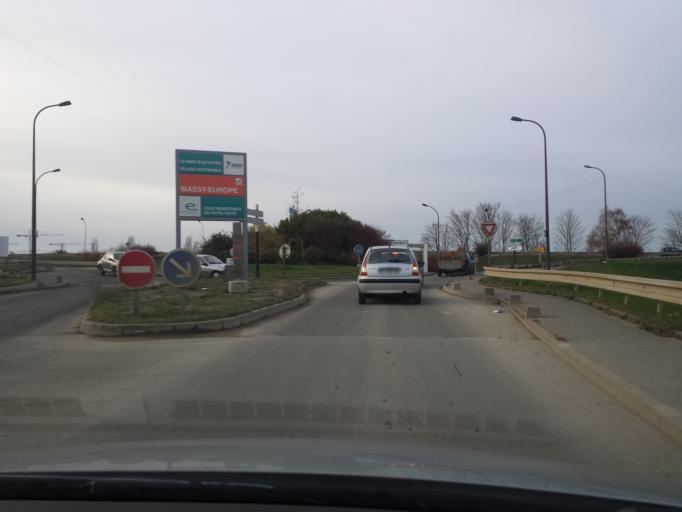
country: FR
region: Ile-de-France
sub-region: Departement de l'Essonne
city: Massy
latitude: 48.7216
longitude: 2.2766
